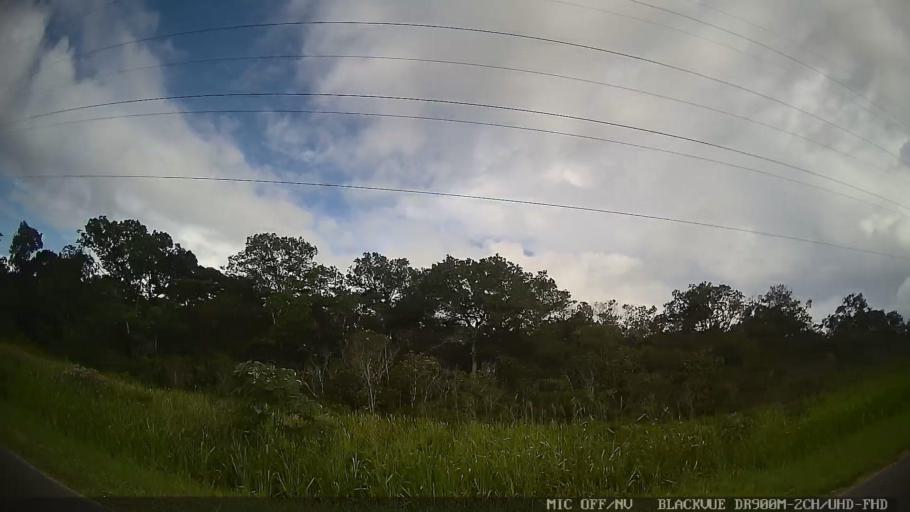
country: BR
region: Sao Paulo
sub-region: Peruibe
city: Peruibe
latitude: -24.2586
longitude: -46.9424
